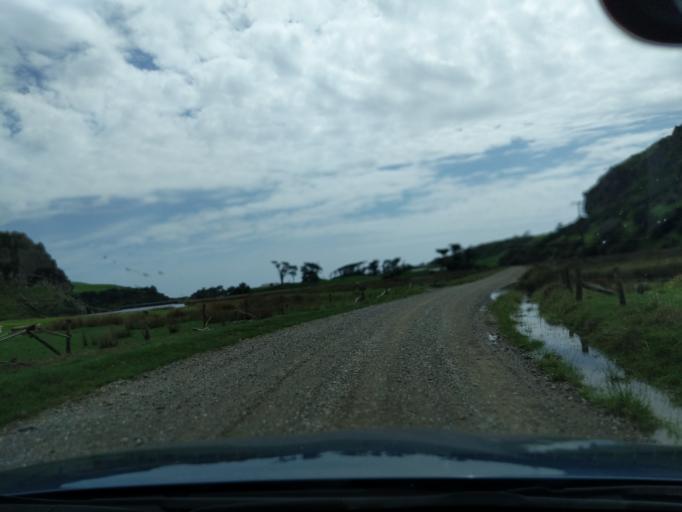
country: NZ
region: Tasman
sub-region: Tasman District
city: Takaka
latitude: -40.6488
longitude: 172.4386
